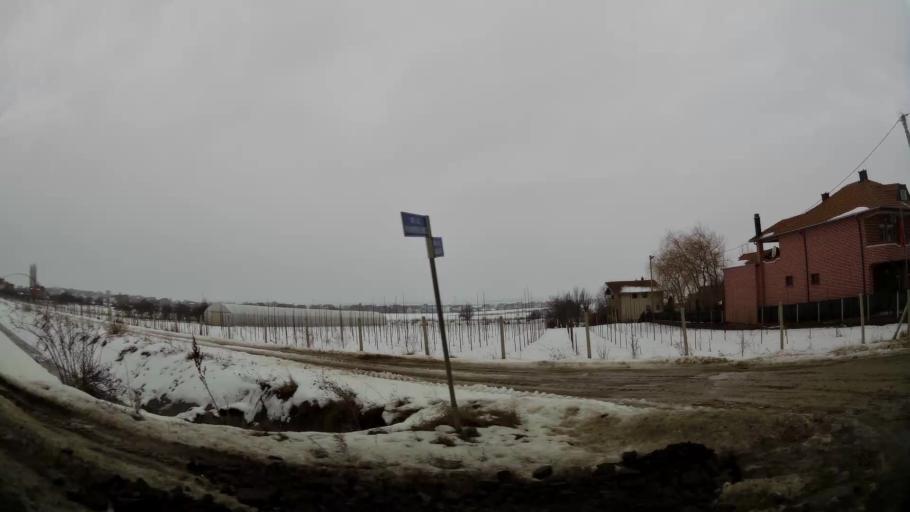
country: XK
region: Pristina
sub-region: Komuna e Prishtines
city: Pristina
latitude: 42.7258
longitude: 21.1446
